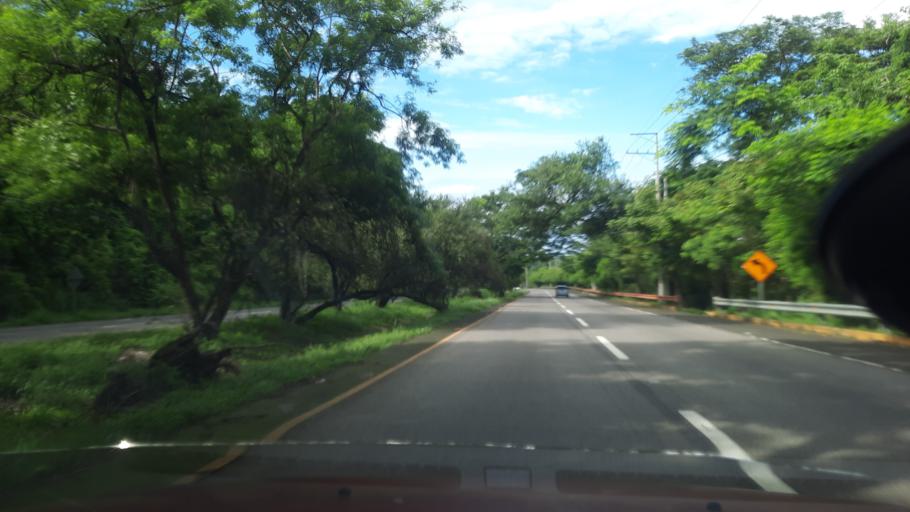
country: SV
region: La Paz
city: Olocuilta
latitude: 13.5327
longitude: -89.1131
